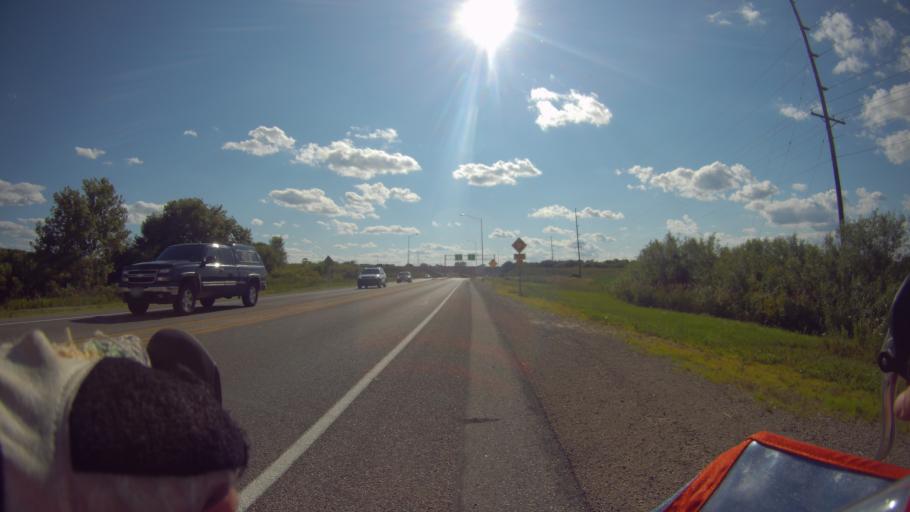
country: US
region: Wisconsin
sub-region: Dane County
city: Oregon
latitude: 42.9179
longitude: -89.3633
